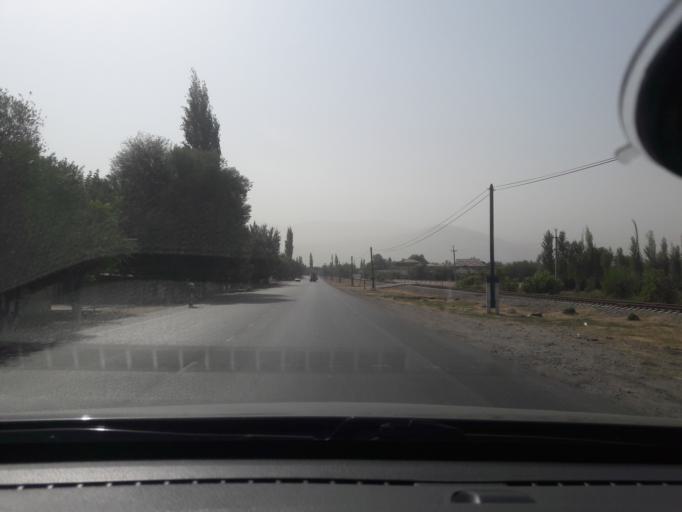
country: TJ
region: Republican Subordination
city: Vahdat
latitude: 38.5240
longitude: 69.0278
